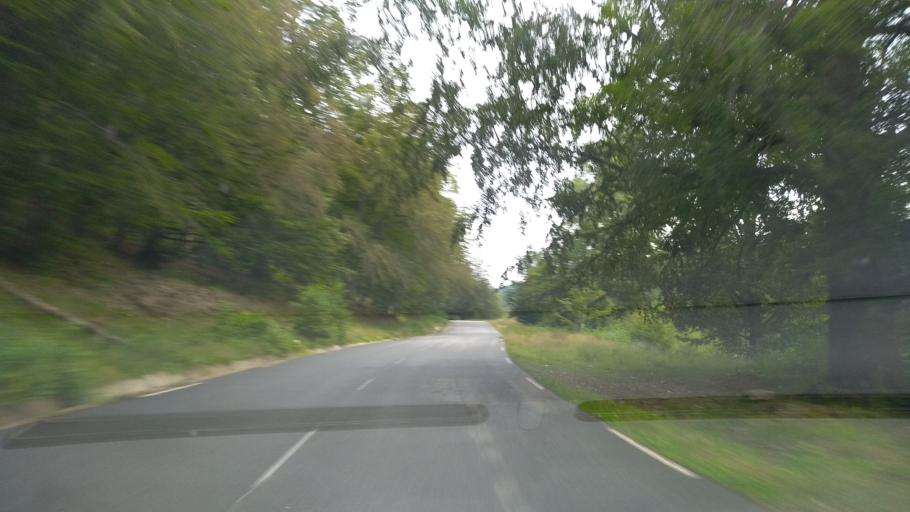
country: RO
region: Hunedoara
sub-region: Municipiul  Vulcan
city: Jiu-Paroseni
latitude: 45.3454
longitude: 23.2907
